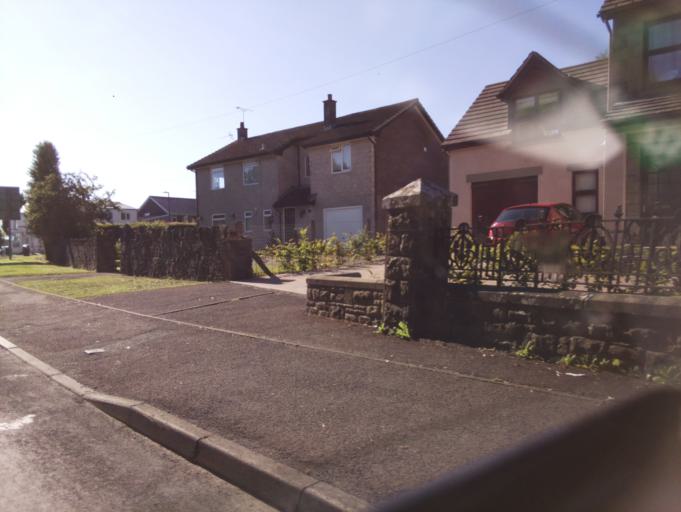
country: GB
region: England
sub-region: Gloucestershire
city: Coleford
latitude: 51.8128
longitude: -2.6219
